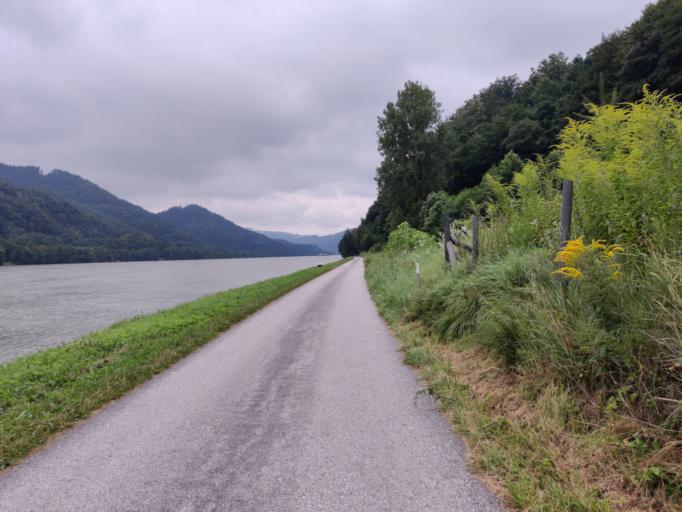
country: AT
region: Lower Austria
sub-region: Politischer Bezirk Melk
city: Nochling
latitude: 48.2245
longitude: 14.9439
